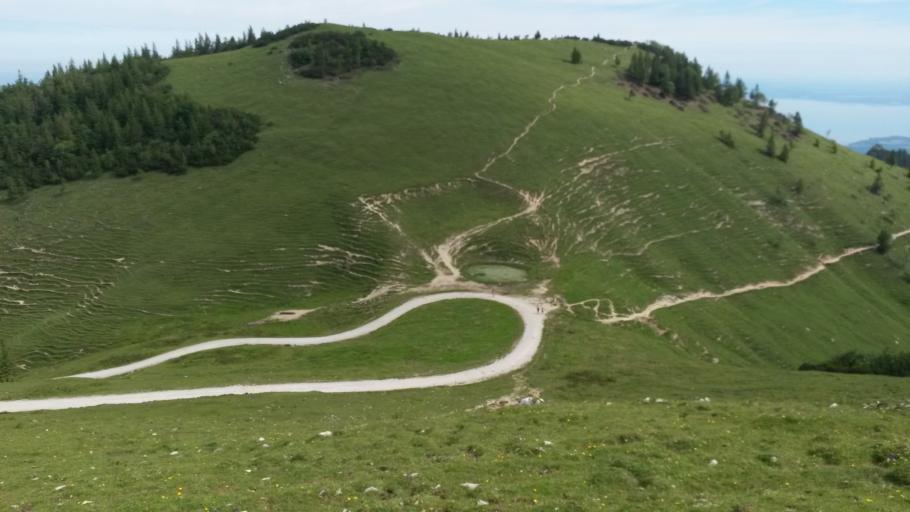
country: DE
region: Bavaria
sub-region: Upper Bavaria
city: Aschau im Chiemgau
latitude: 47.7592
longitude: 12.3670
